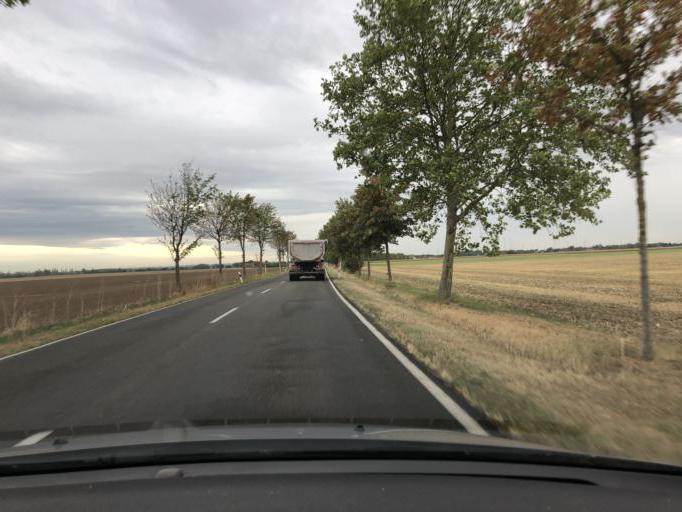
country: DE
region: Saxony-Anhalt
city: Nienburg/Saale
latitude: 51.8451
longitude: 11.7288
